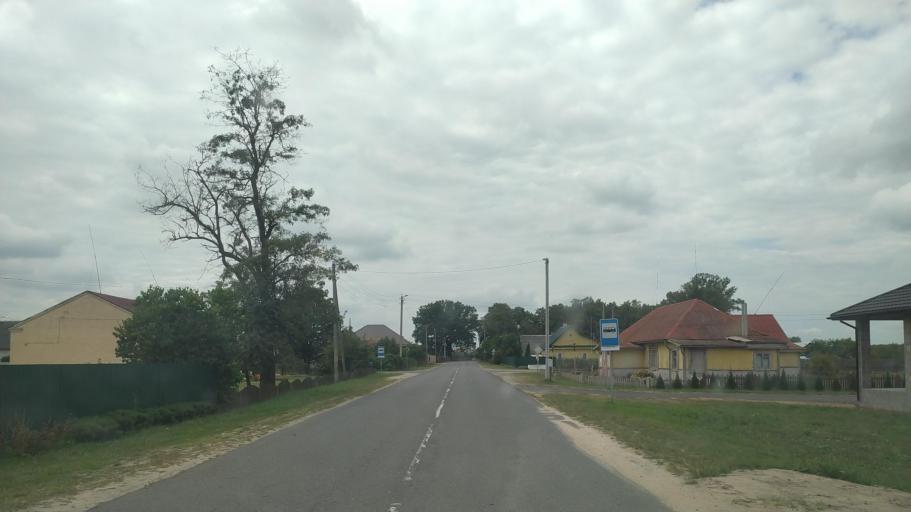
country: BY
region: Brest
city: Byelaazyorsk
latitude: 52.5400
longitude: 25.0923
